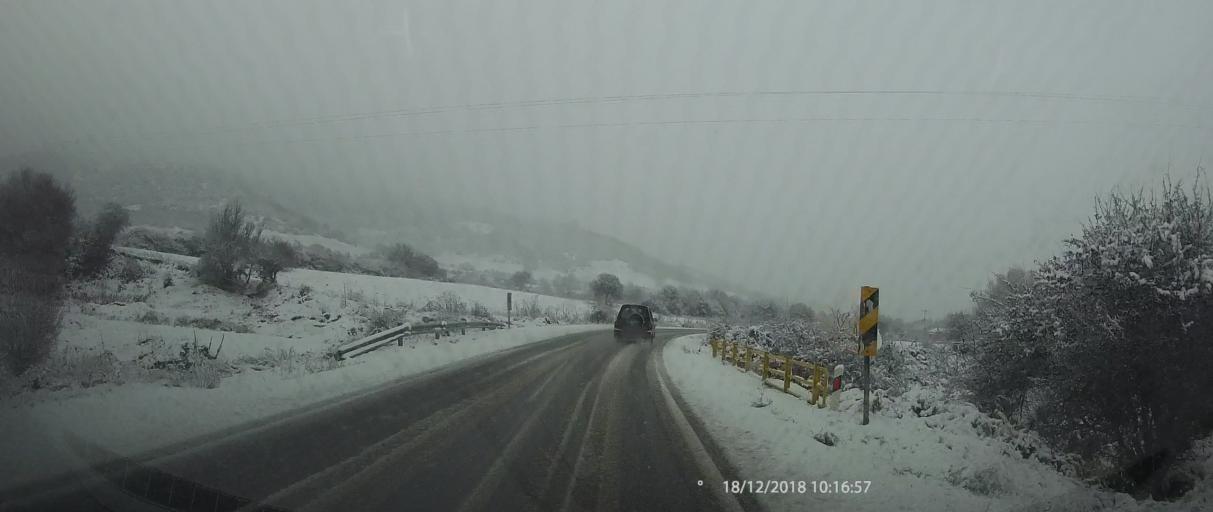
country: GR
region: Thessaly
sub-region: Nomos Larisis
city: Livadi
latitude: 40.1202
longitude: 22.2107
